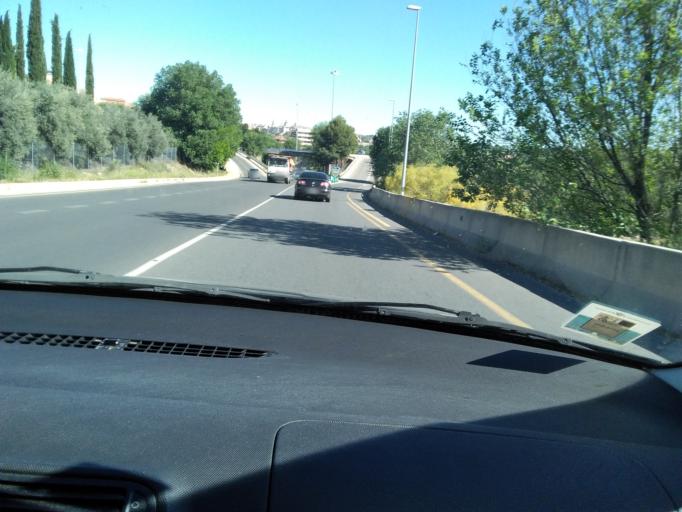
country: ES
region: Castille-La Mancha
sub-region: Province of Toledo
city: Toledo
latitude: 39.8766
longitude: -4.0440
